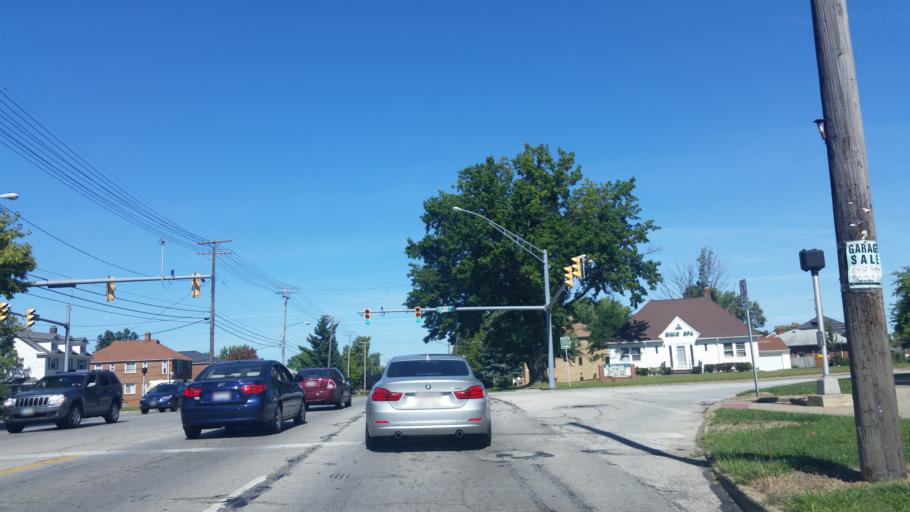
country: US
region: Ohio
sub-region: Cuyahoga County
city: Parma
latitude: 41.3869
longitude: -81.7345
